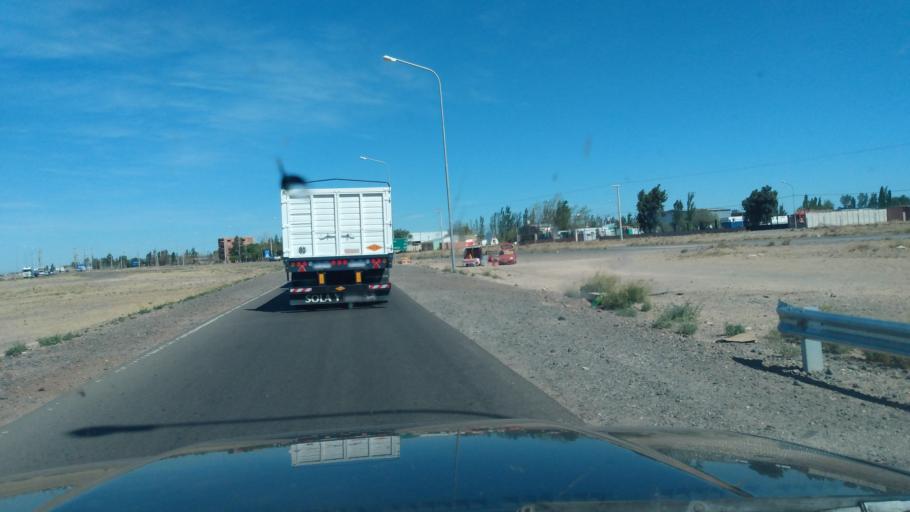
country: AR
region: Neuquen
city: Neuquen
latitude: -38.9111
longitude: -68.1223
